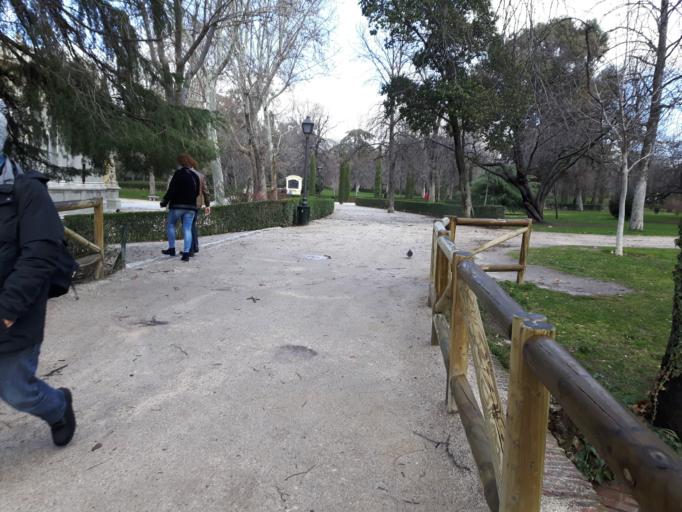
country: ES
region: Madrid
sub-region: Provincia de Madrid
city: Retiro
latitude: 40.4168
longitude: -3.6826
